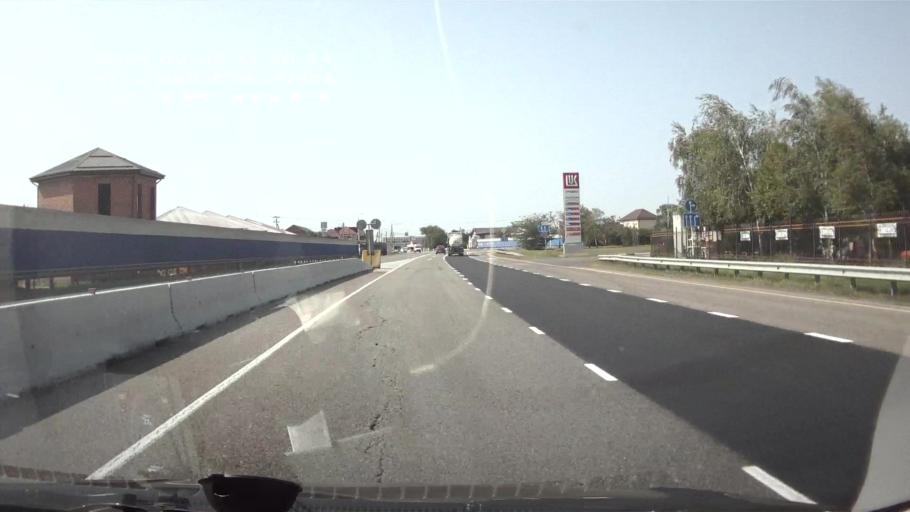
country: RU
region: Adygeya
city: Khatukay
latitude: 45.2189
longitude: 39.5878
